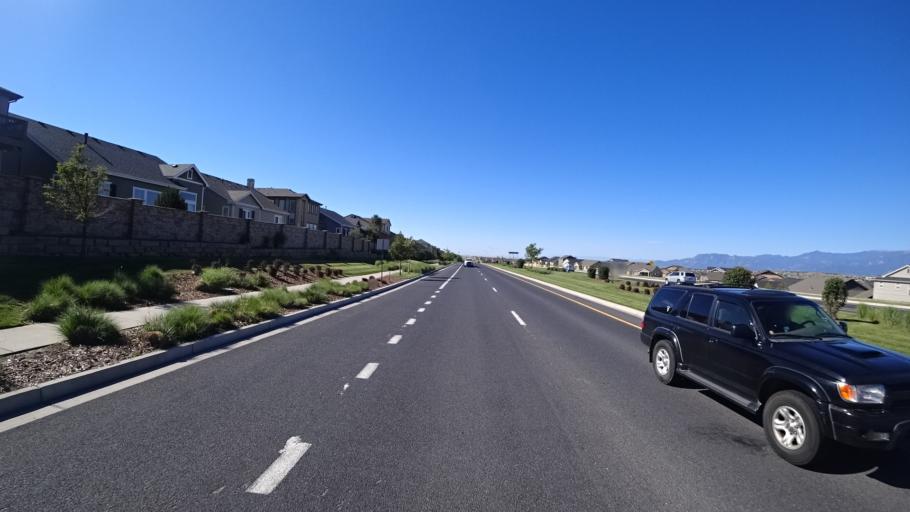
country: US
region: Colorado
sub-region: El Paso County
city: Cimarron Hills
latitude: 38.9330
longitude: -104.6826
